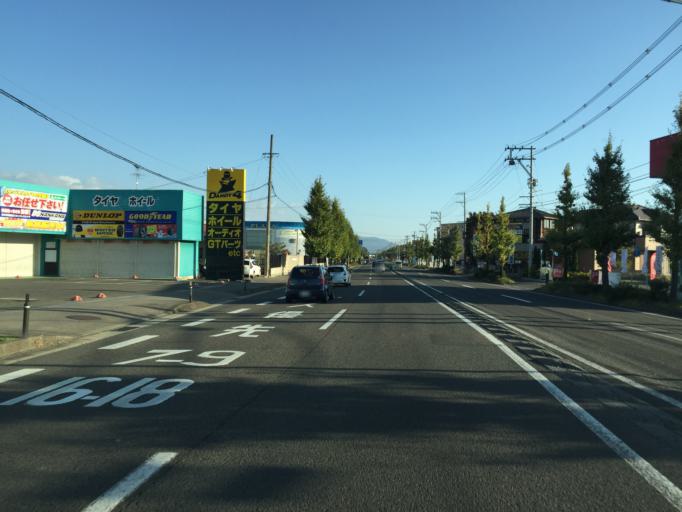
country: JP
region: Fukushima
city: Hobaramachi
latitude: 37.8120
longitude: 140.4990
